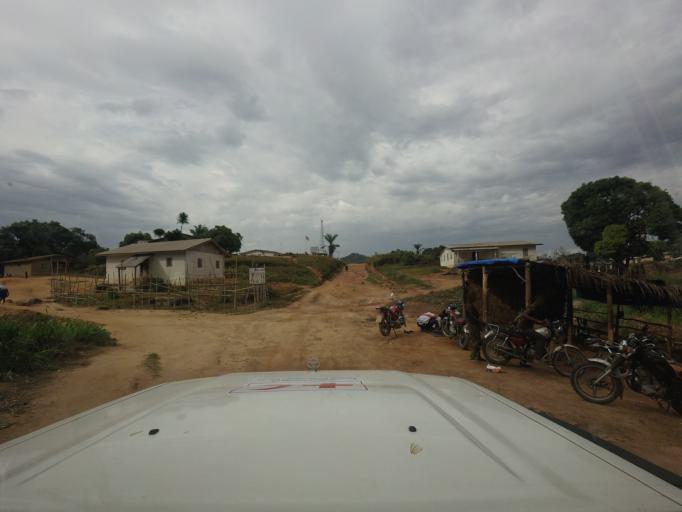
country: SL
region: Eastern Province
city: Buedu
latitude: 8.2828
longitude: -10.0854
